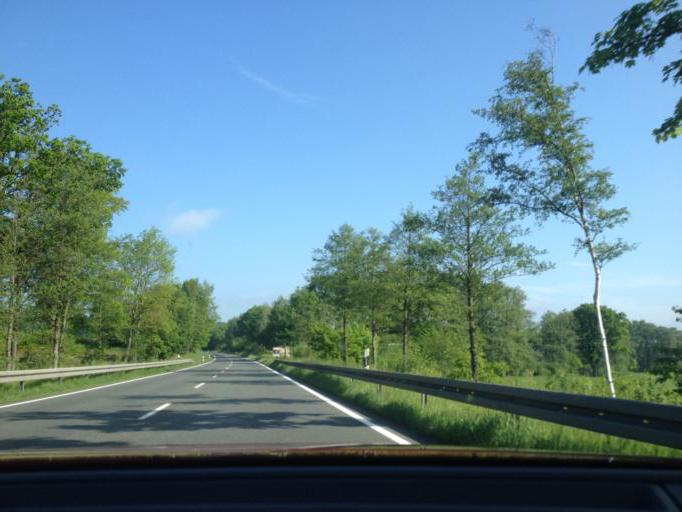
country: DE
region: Bavaria
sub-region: Upper Palatinate
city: Kemnath
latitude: 49.8504
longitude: 11.8871
